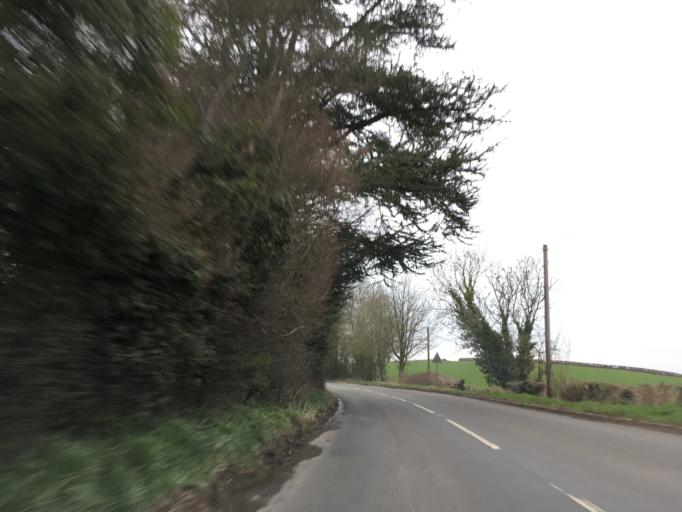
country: GB
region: Wales
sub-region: Monmouthshire
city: Llangybi
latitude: 51.6542
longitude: -2.9114
